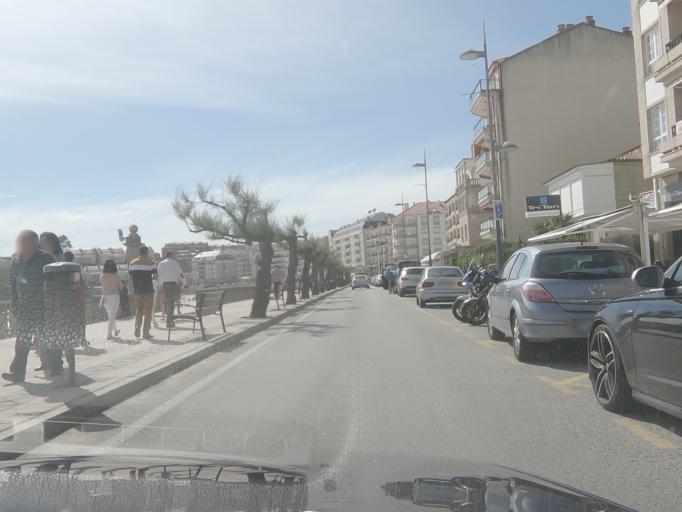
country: ES
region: Galicia
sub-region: Provincia de Pontevedra
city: Sanxenxo
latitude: 42.4013
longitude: -8.8108
